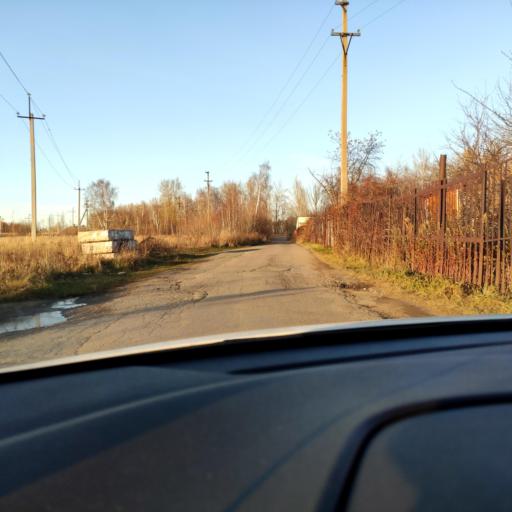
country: RU
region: Tatarstan
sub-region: Gorod Kazan'
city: Kazan
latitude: 55.9046
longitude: 49.0651
